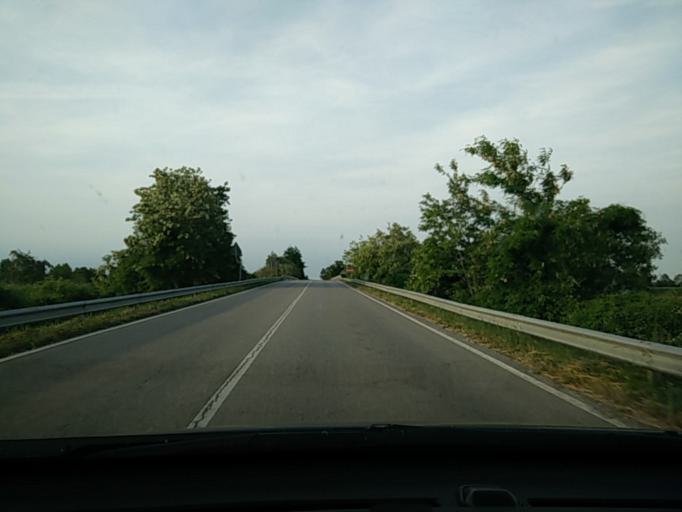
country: IT
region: Veneto
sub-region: Provincia di Venezia
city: San Liberale
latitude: 45.5608
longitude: 12.3533
